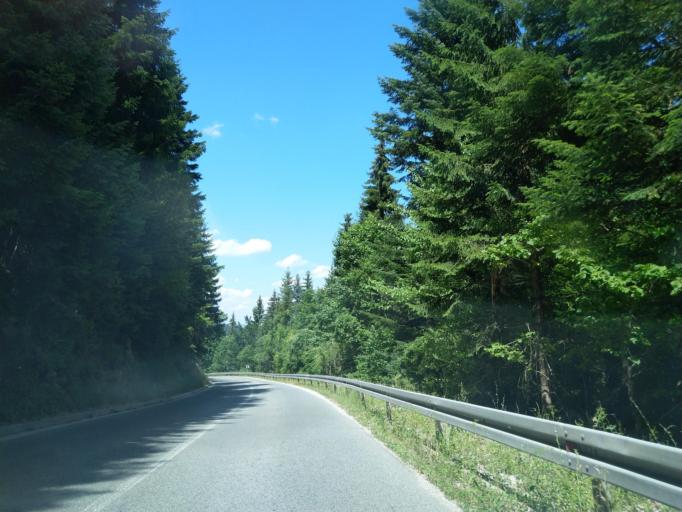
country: RS
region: Central Serbia
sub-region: Zlatiborski Okrug
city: Nova Varos
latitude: 43.4162
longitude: 19.8299
